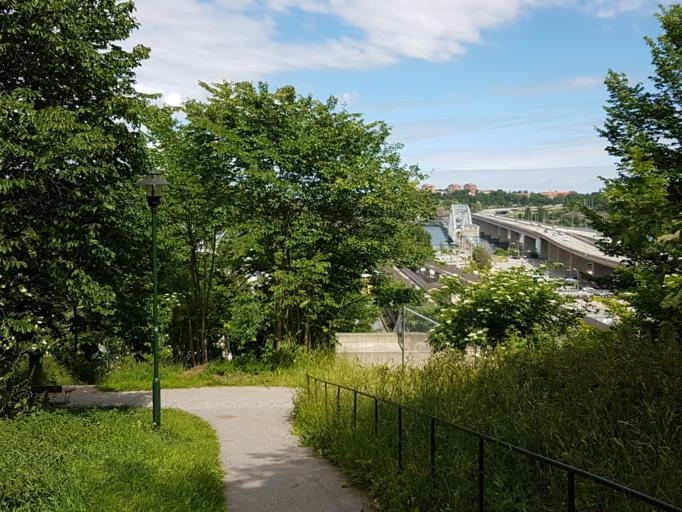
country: SE
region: Stockholm
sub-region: Stockholms Kommun
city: OEstermalm
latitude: 59.3567
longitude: 18.1009
